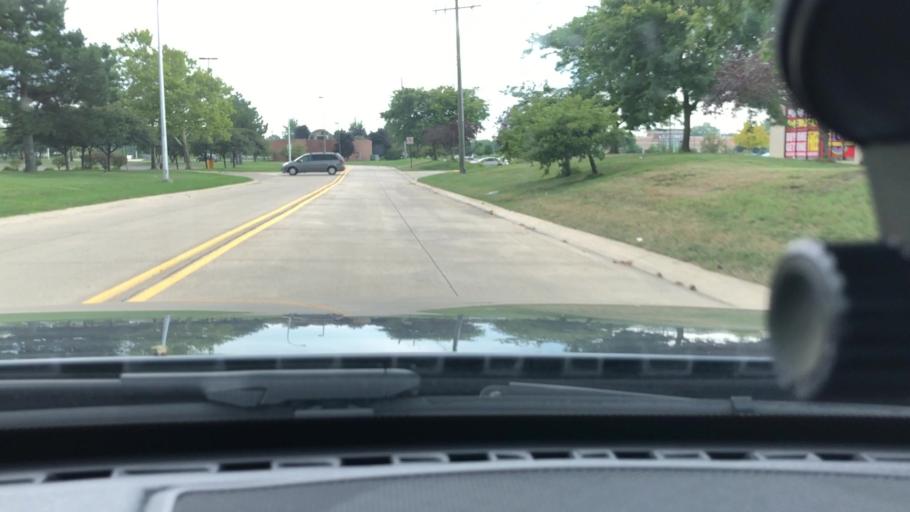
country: US
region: Michigan
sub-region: Wayne County
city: Livonia
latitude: 42.3713
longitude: -83.3404
